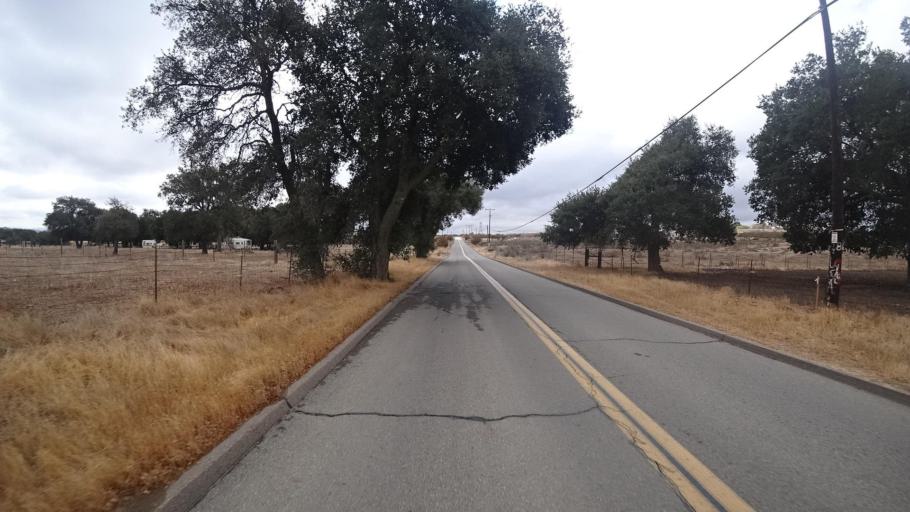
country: MX
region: Baja California
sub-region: Tecate
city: Cereso del Hongo
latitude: 32.6142
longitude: -116.3203
